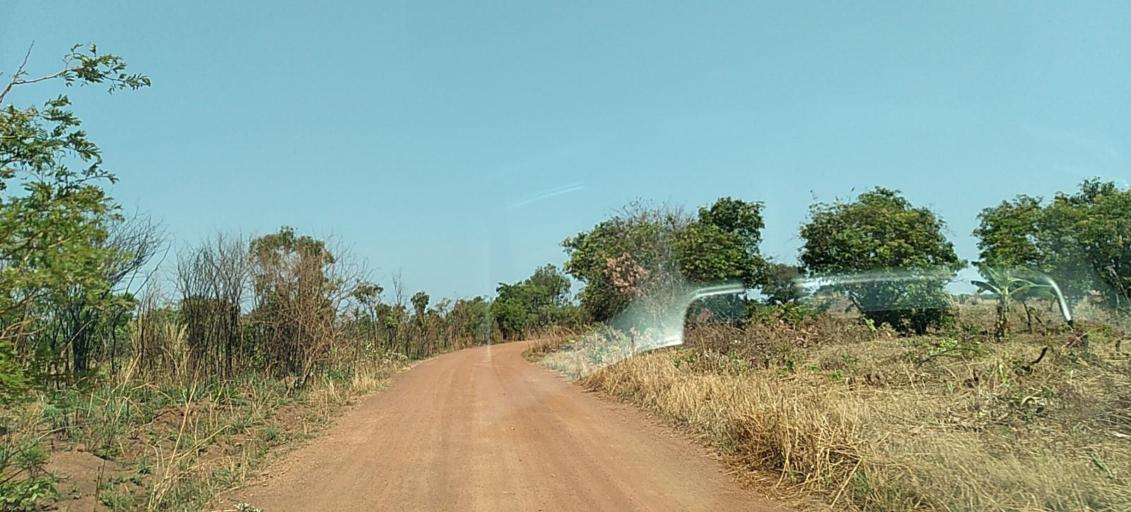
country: ZM
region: Copperbelt
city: Chingola
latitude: -12.5397
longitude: 27.7303
